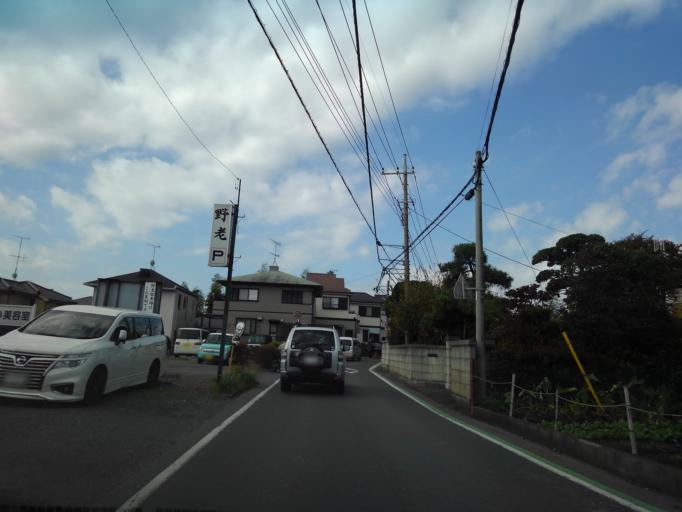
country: JP
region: Saitama
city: Tokorozawa
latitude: 35.7789
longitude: 139.4687
